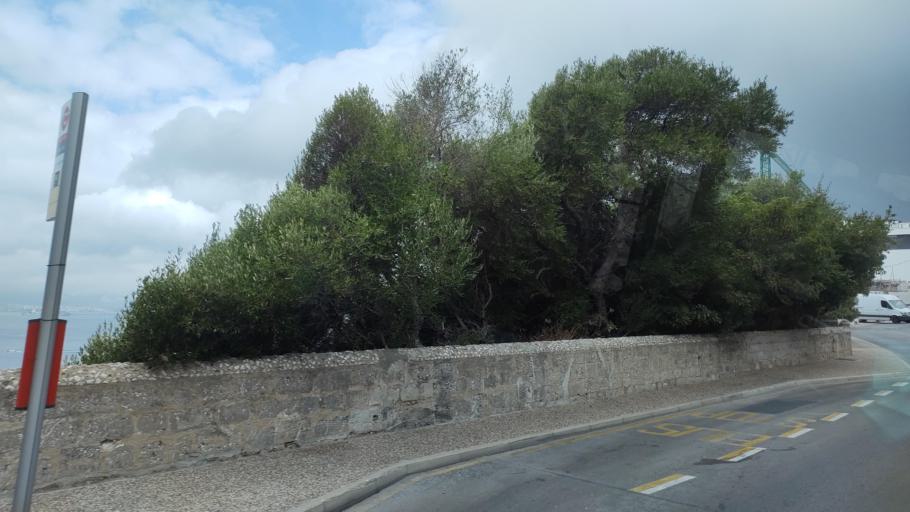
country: GI
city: Gibraltar
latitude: 36.1156
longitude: -5.3481
